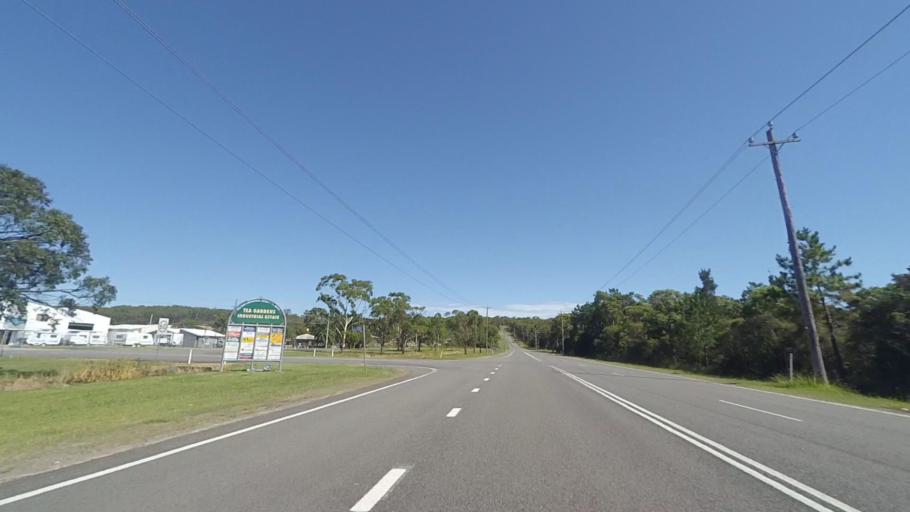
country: AU
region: New South Wales
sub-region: Great Lakes
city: Hawks Nest
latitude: -32.6457
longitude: 152.1469
